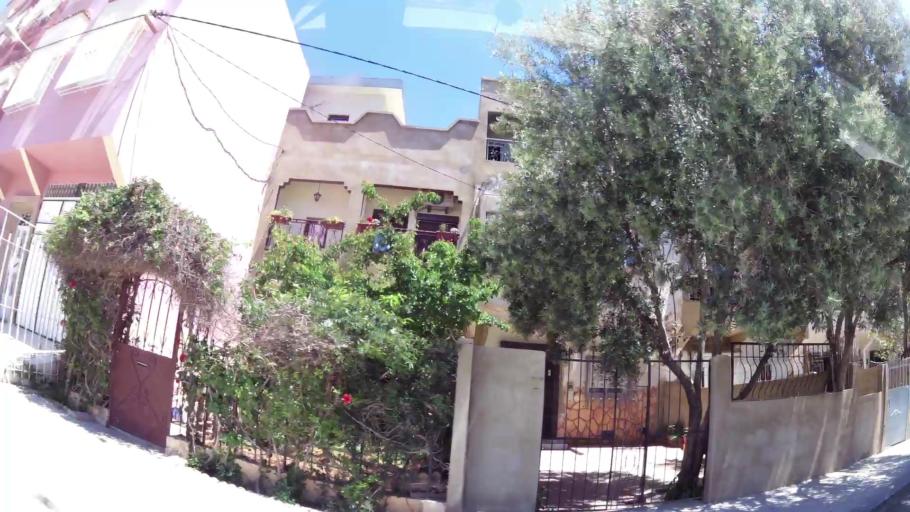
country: MA
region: Meknes-Tafilalet
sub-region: Meknes
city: Meknes
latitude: 33.9085
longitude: -5.5589
